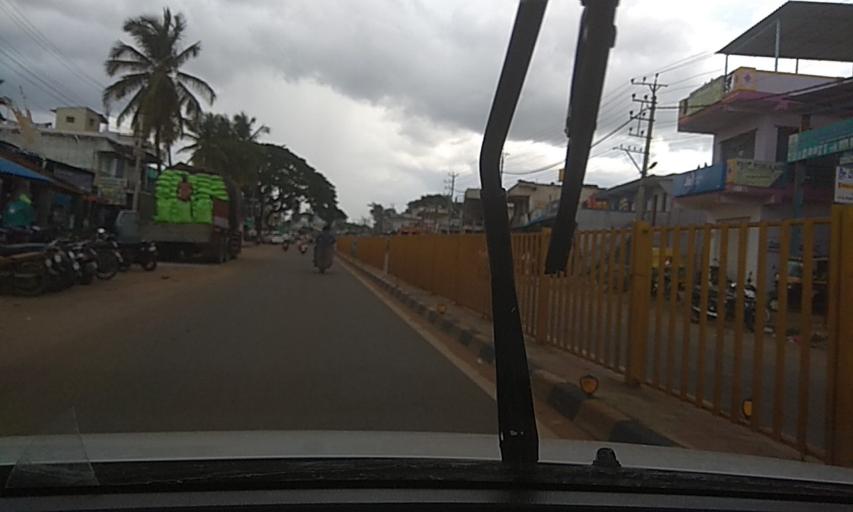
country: IN
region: Karnataka
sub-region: Tumkur
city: Kunigal
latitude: 13.1567
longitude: 77.0306
